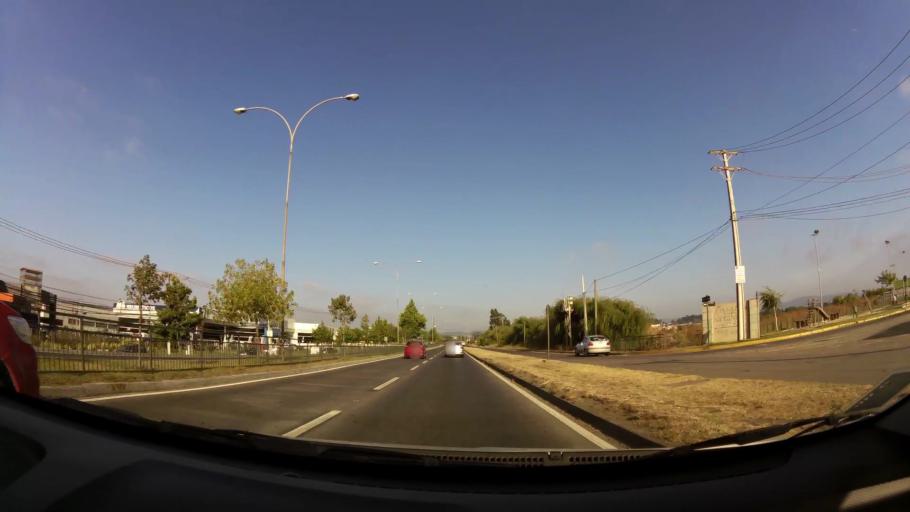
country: CL
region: Biobio
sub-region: Provincia de Concepcion
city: Concepcion
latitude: -36.7846
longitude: -73.0796
